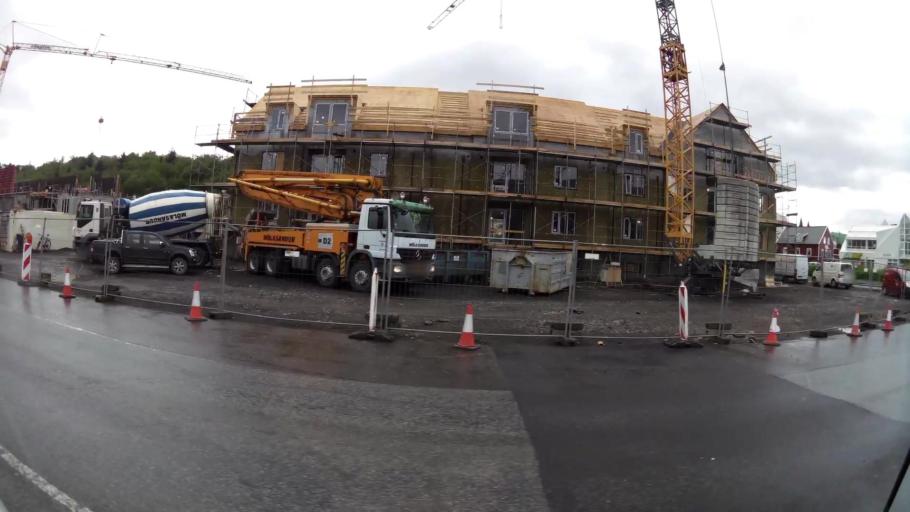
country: IS
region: Northeast
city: Akureyri
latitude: 65.6801
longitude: -18.0876
